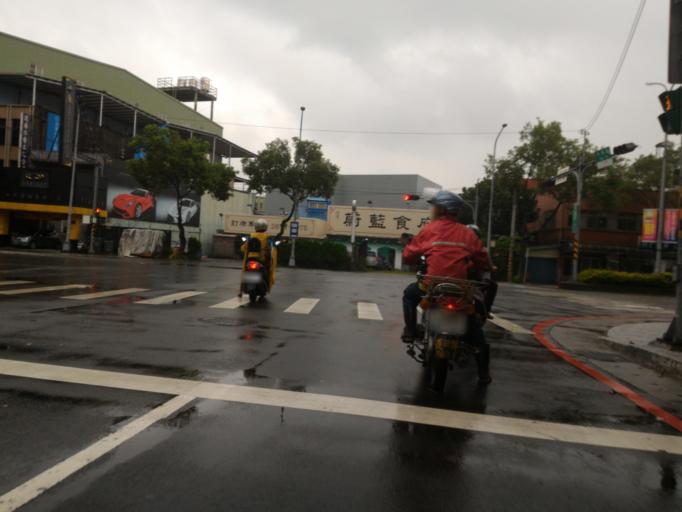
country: TW
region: Taiwan
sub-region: Taoyuan
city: Taoyuan
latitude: 24.9443
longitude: 121.3807
